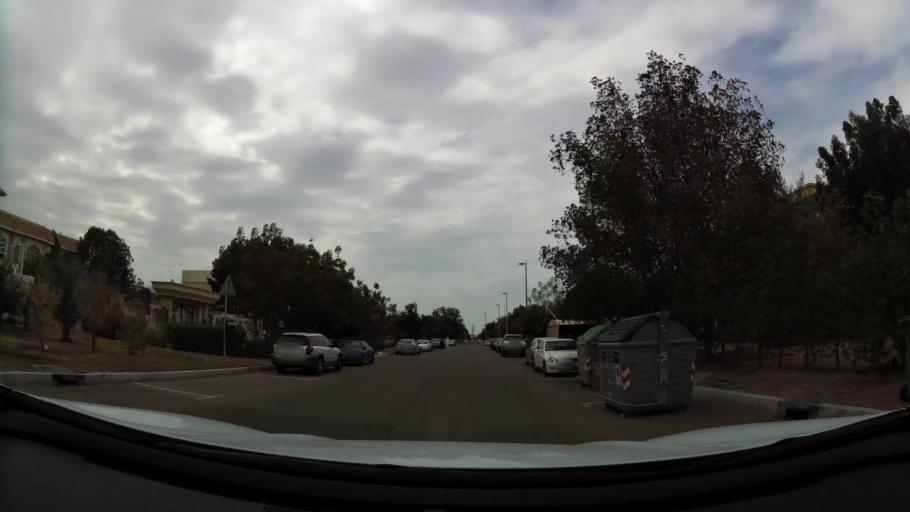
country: AE
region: Abu Dhabi
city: Abu Dhabi
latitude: 24.4270
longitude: 54.4129
